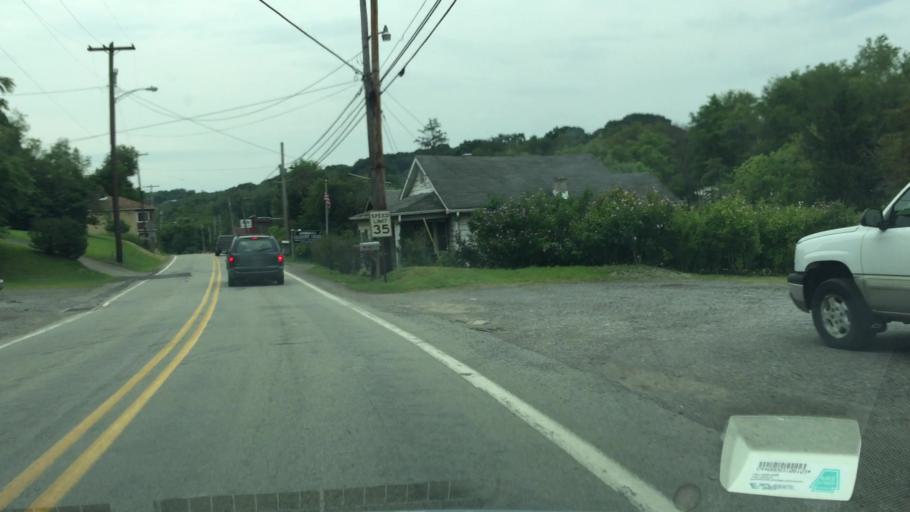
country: US
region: Pennsylvania
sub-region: Allegheny County
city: Curtisville
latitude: 40.6415
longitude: -79.8507
